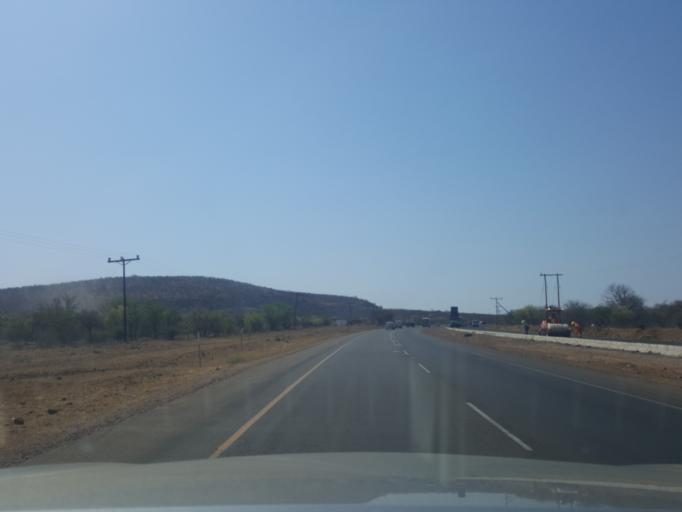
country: BW
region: Kweneng
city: Gabane
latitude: -24.7574
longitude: 25.8298
